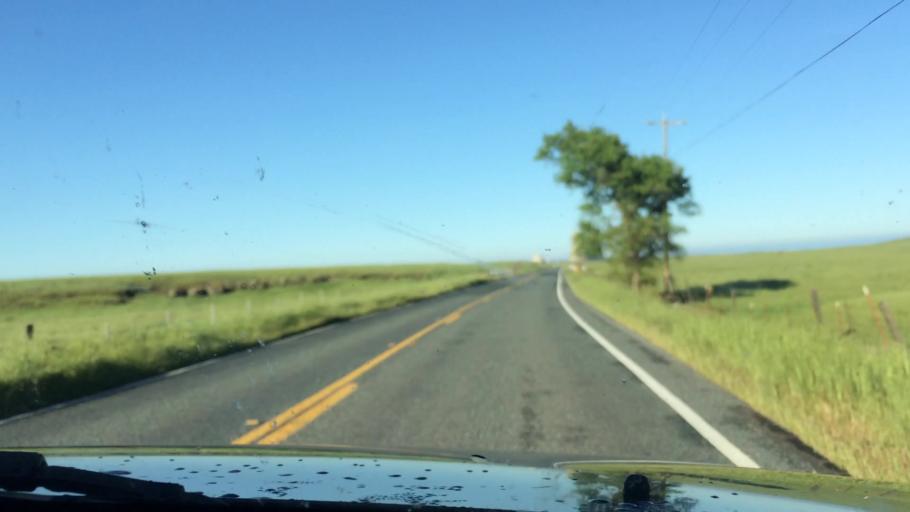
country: US
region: California
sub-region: Sacramento County
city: Clay
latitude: 38.3606
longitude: -121.0841
